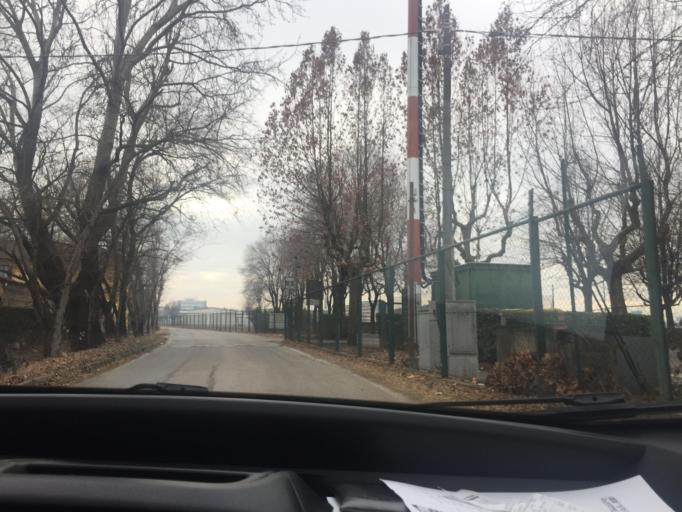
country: IT
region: Piedmont
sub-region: Provincia di Torino
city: Savonera
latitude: 45.0865
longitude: 7.6114
